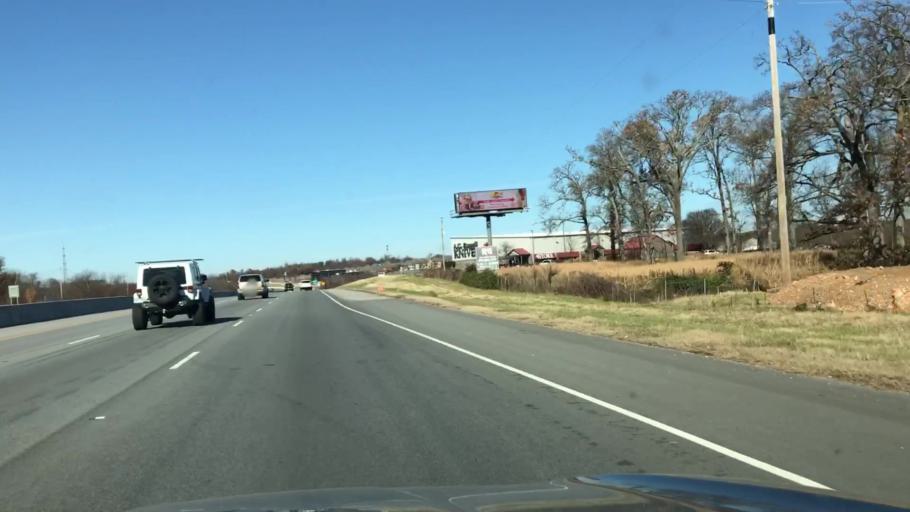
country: US
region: Arkansas
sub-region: Benton County
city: Lowell
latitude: 36.2879
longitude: -94.1596
